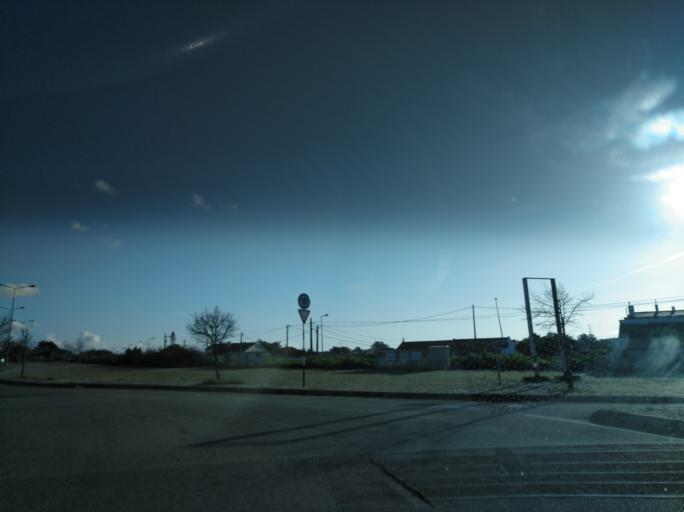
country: PT
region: Setubal
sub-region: Almada
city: Sobreda
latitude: 38.6556
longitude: -9.1887
